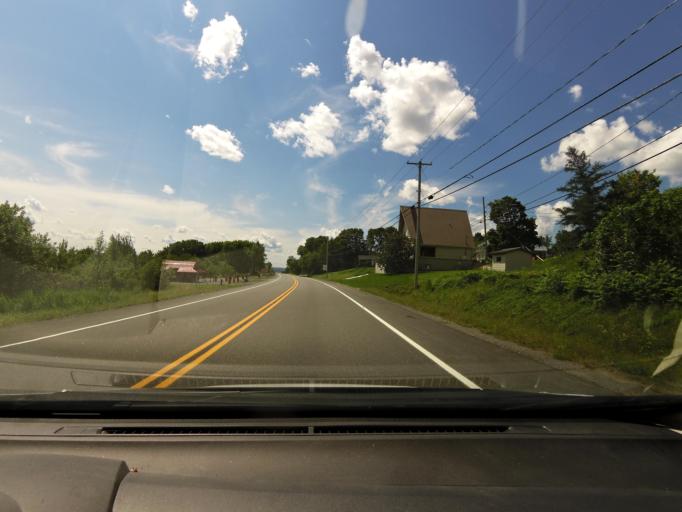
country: CA
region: Quebec
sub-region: Capitale-Nationale
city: Neuville
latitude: 46.7109
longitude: -71.5601
